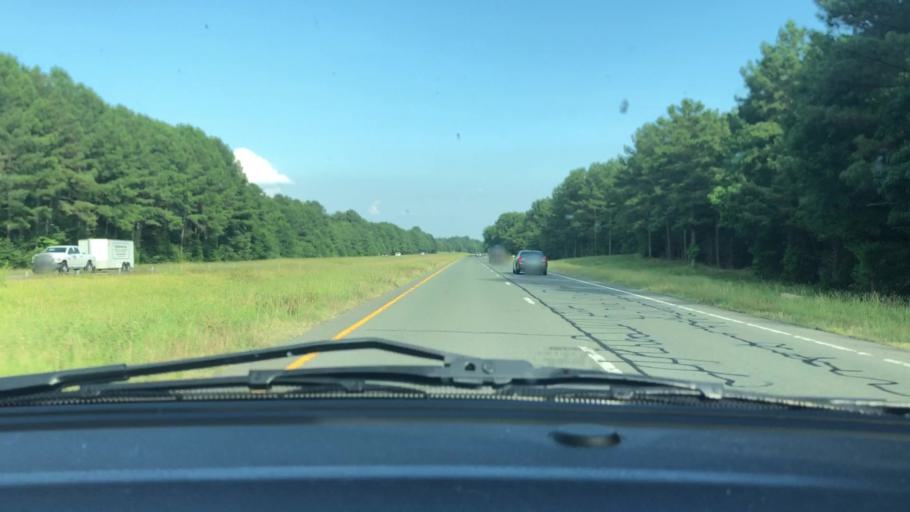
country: US
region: North Carolina
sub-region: Chatham County
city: Siler City
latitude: 35.7480
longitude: -79.4459
